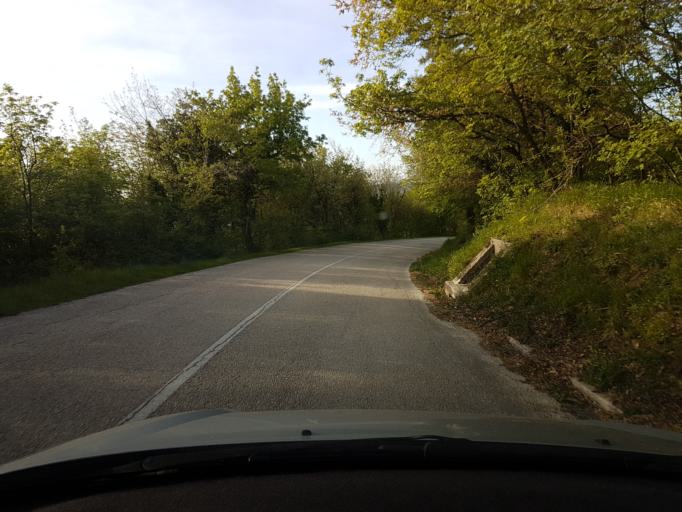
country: IT
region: Friuli Venezia Giulia
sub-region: Provincia di Trieste
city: Dolina
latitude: 45.5885
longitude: 13.8523
